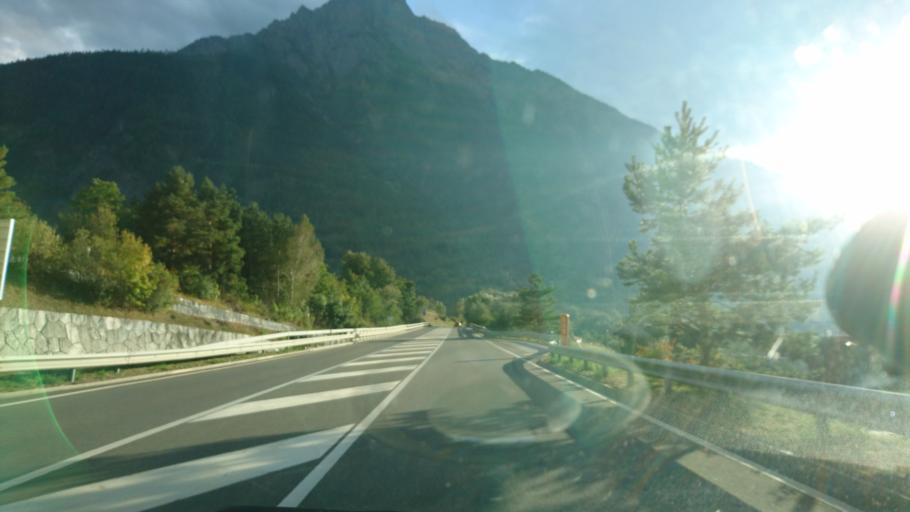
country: CH
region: Valais
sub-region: Brig District
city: Naters
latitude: 46.3114
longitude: 8.0007
